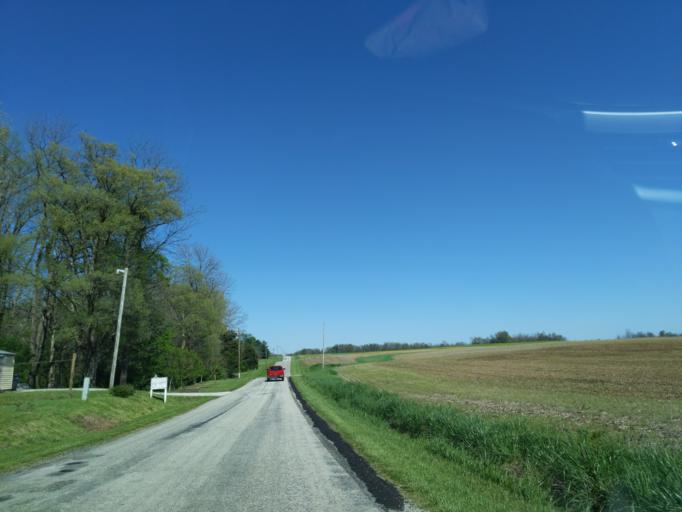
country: US
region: Indiana
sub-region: Decatur County
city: Greensburg
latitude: 39.2928
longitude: -85.4808
